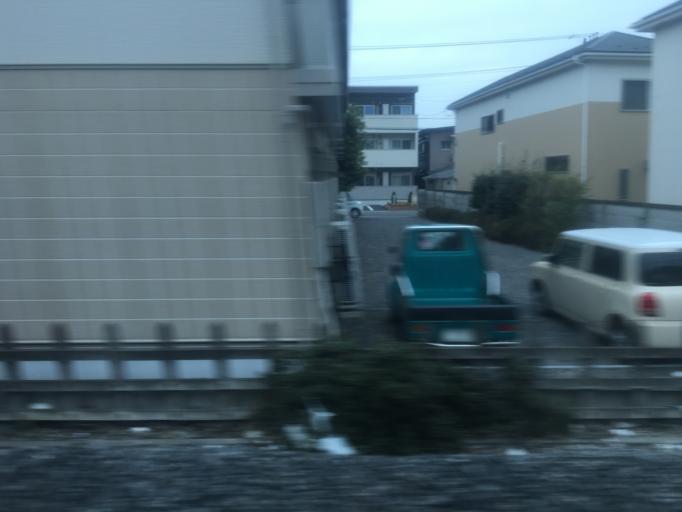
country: JP
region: Saitama
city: Okegawa
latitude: 35.9958
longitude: 139.5673
